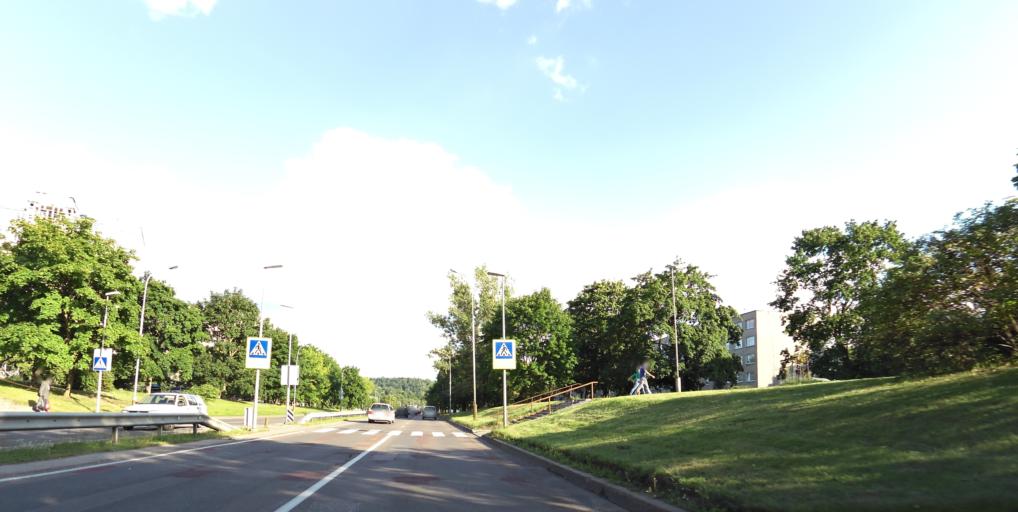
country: LT
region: Vilnius County
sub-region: Vilnius
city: Vilnius
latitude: 54.6991
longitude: 25.2943
